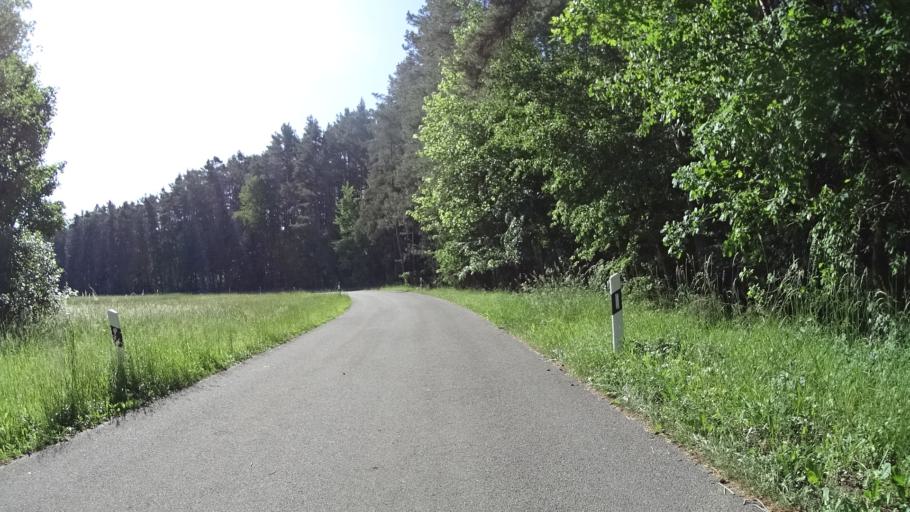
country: DE
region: Bavaria
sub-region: Regierungsbezirk Mittelfranken
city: Arberg
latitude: 49.1578
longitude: 10.5818
